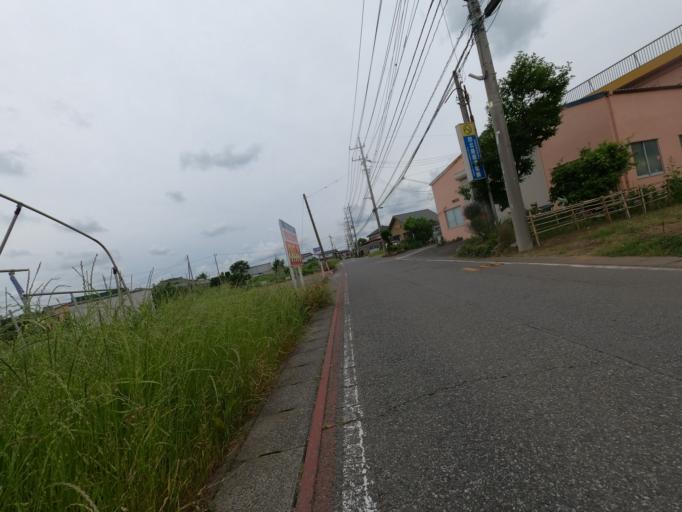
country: JP
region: Ibaraki
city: Moriya
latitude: 35.9503
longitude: 139.9712
